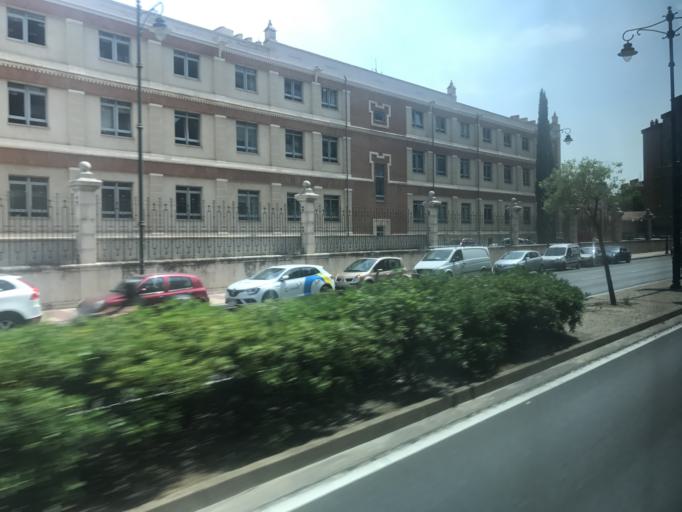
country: ES
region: Castille and Leon
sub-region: Provincia de Valladolid
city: Valladolid
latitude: 41.6437
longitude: -4.7342
